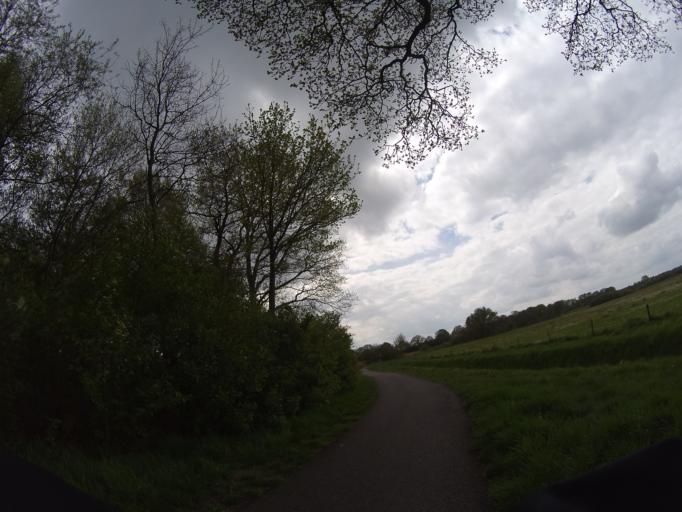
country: NL
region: Overijssel
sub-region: Gemeente Hardenberg
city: Hardenberg
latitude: 52.5571
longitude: 6.6021
